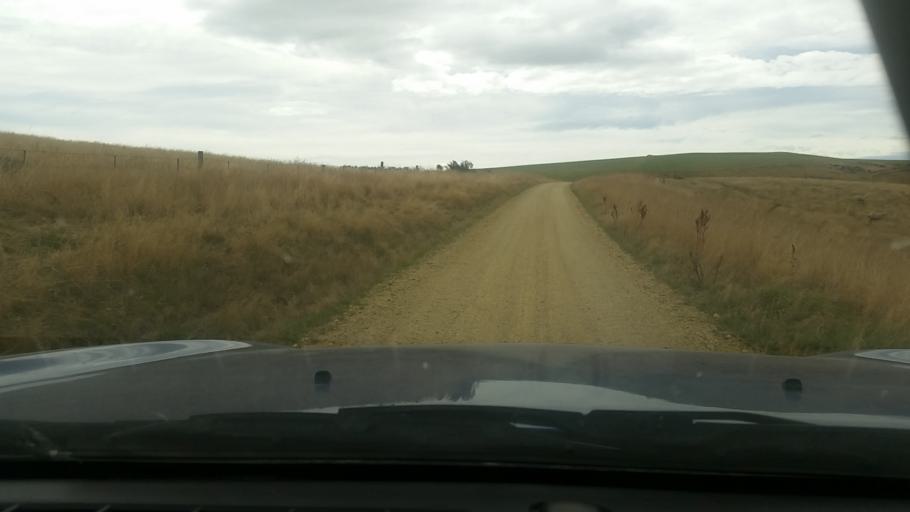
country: NZ
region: Southland
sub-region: Gore District
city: Gore
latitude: -45.5827
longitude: 169.3992
